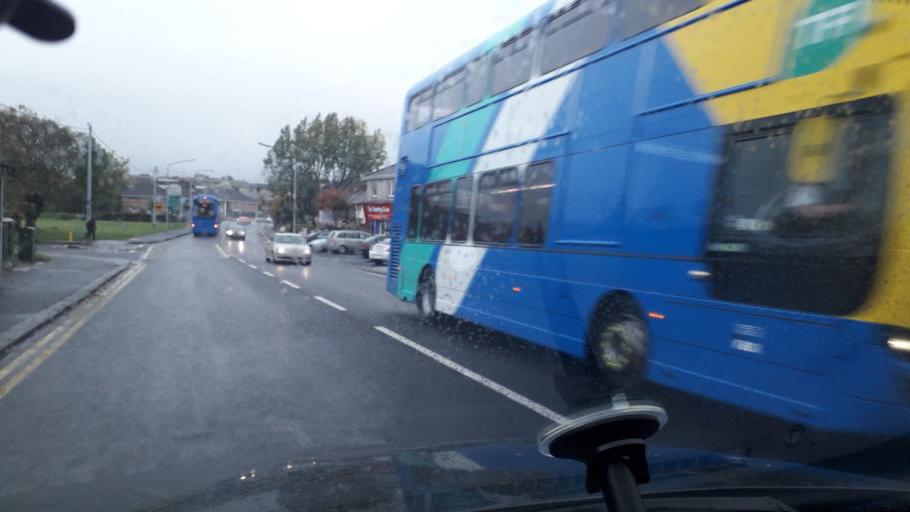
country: IE
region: Leinster
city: Oldbawn
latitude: 53.2845
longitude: -6.3604
